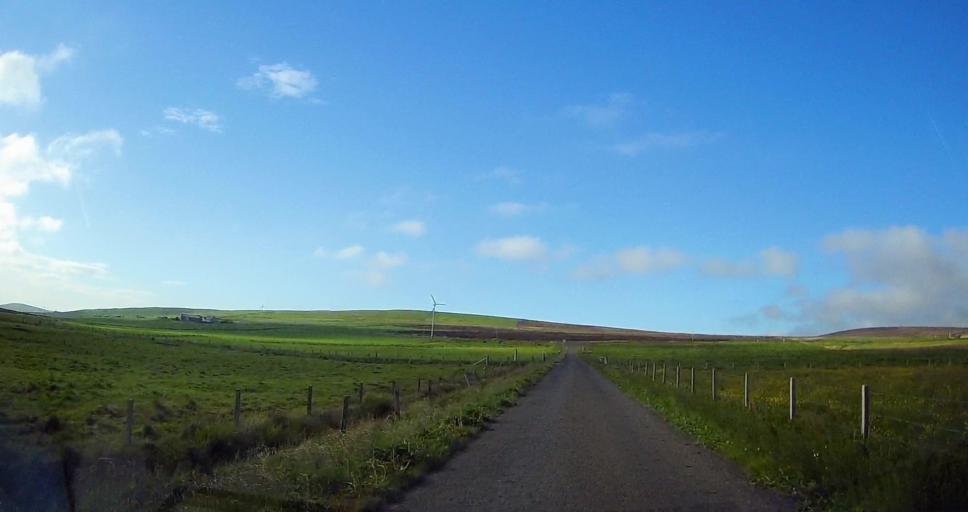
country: GB
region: Scotland
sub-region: Orkney Islands
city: Stromness
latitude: 59.0894
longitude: -3.1831
